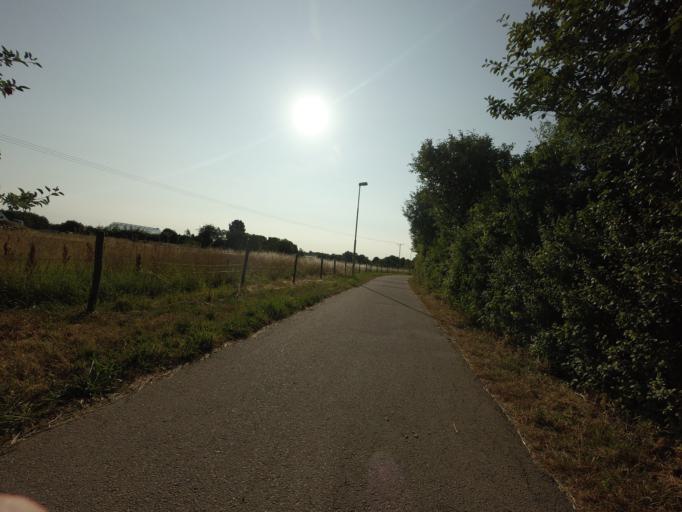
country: SE
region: Skane
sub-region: Landskrona
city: Asmundtorp
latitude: 55.8598
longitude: 12.8948
